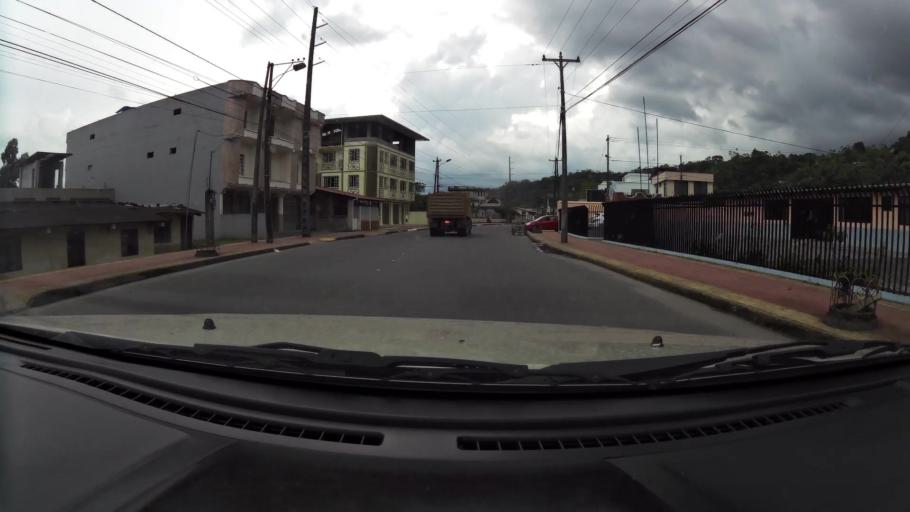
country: EC
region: Pastaza
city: Puyo
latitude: -1.4917
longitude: -78.0148
